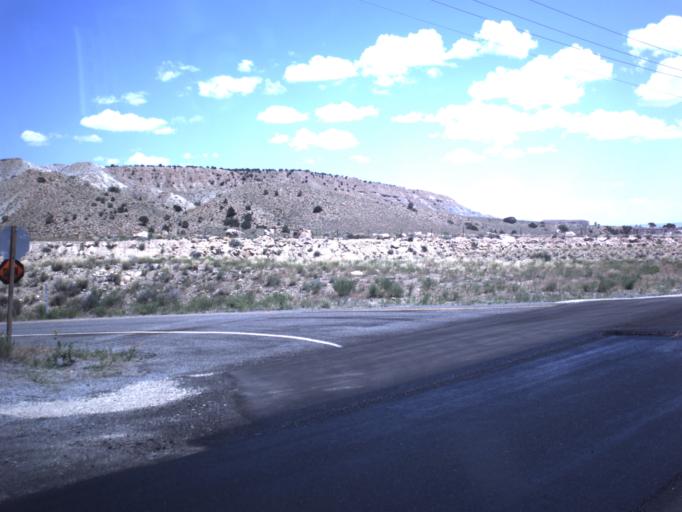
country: US
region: Utah
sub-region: Emery County
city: Orangeville
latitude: 39.2553
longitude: -111.0988
